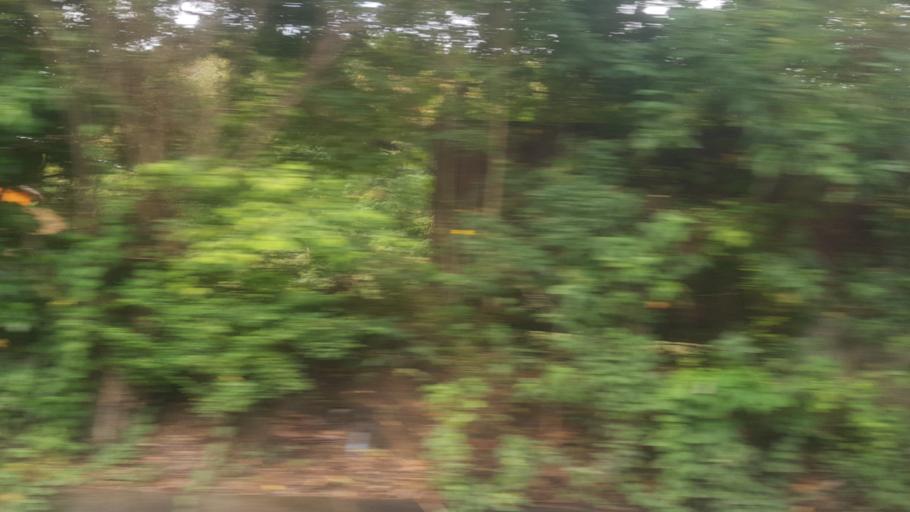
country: LC
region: Castries Quarter
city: Bisee
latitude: 14.0307
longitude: -60.9665
